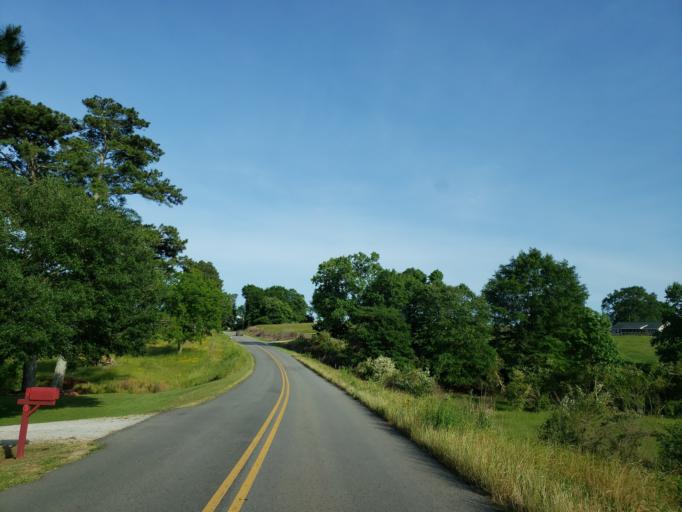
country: US
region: Georgia
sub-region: Carroll County
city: Bowdon
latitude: 33.5018
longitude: -85.3269
